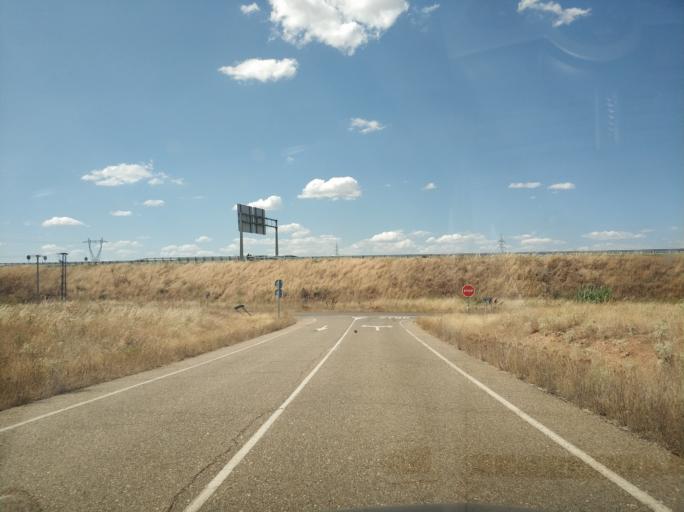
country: ES
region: Castille and Leon
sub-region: Provincia de Salamanca
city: Aldeatejada
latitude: 40.9444
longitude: -5.6957
